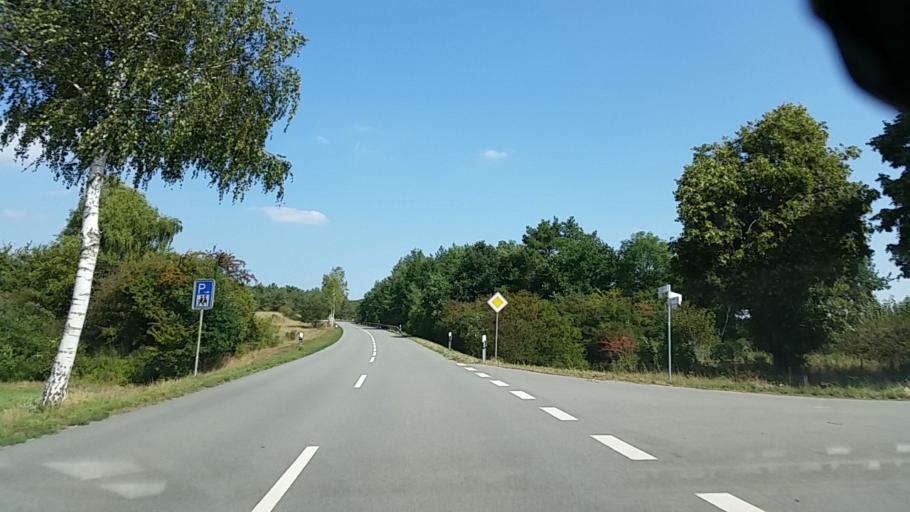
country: DE
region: Lower Saxony
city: Bienenbuttel
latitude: 53.1675
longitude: 10.5145
